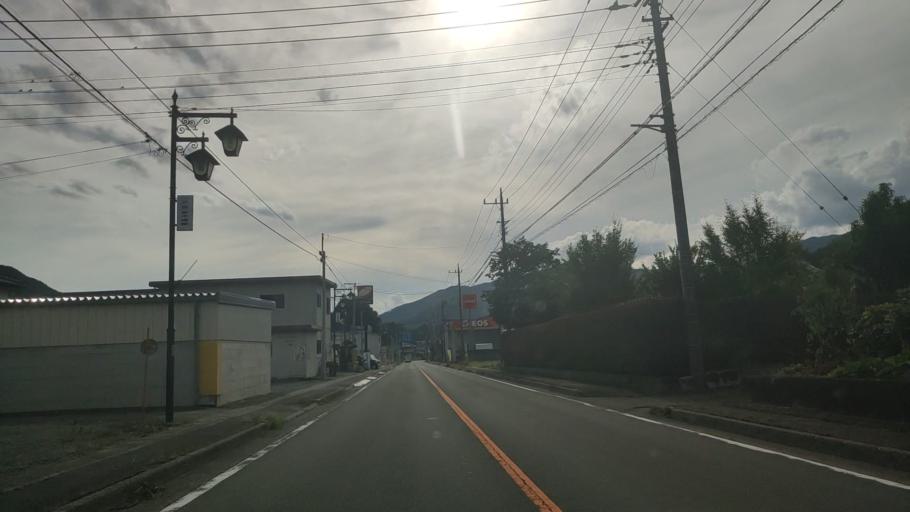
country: JP
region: Gunma
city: Omamacho-omama
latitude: 36.5401
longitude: 139.3542
